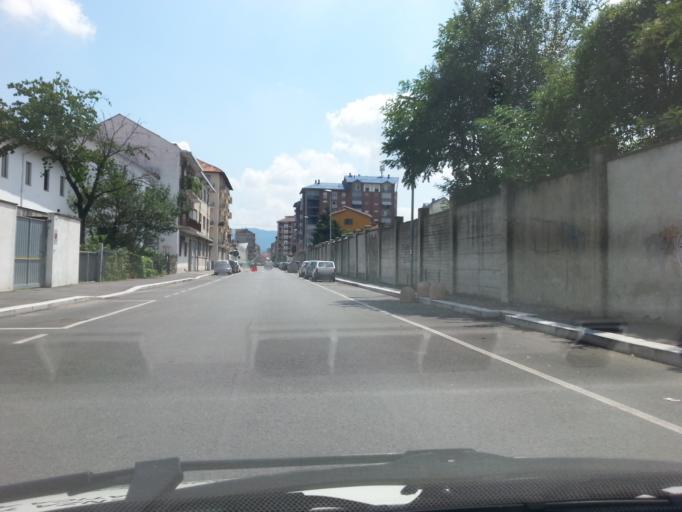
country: IT
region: Piedmont
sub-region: Provincia di Torino
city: Turin
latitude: 45.0975
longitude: 7.6862
